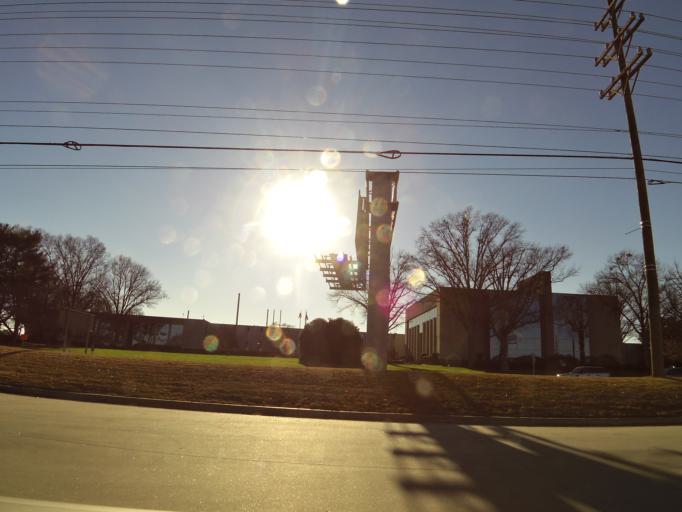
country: US
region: South Carolina
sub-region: Spartanburg County
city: Wellford
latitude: 34.9127
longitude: -82.1055
